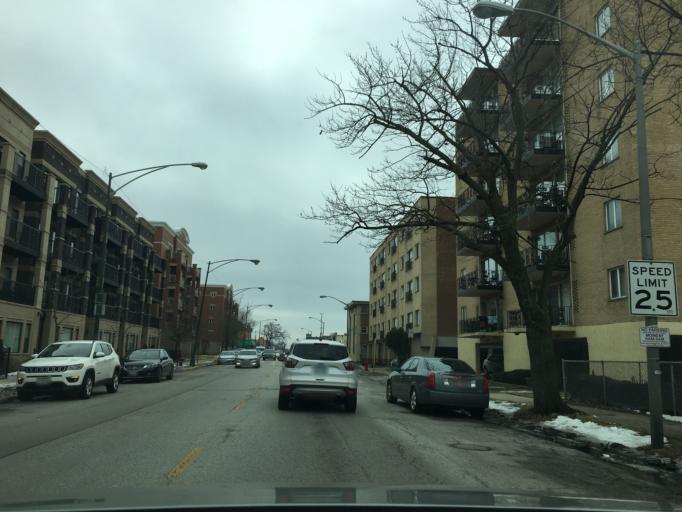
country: US
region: Illinois
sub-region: Cook County
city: Elmwood Park
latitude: 41.9341
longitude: -87.8066
